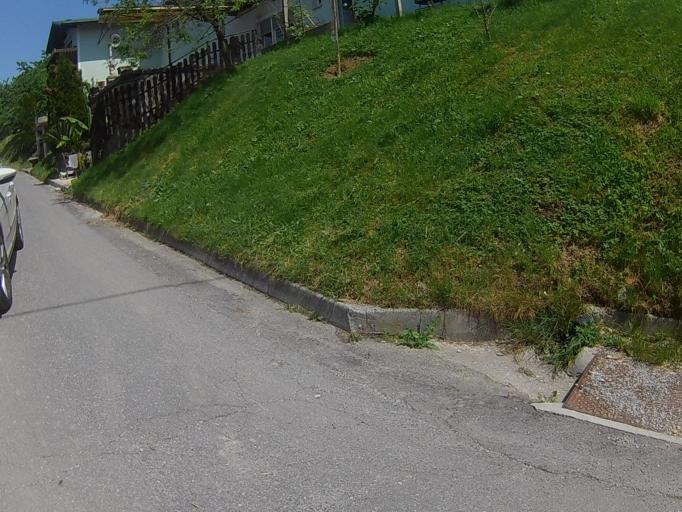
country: SI
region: Pesnica
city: Pesnica pri Mariboru
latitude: 46.5797
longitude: 15.6724
